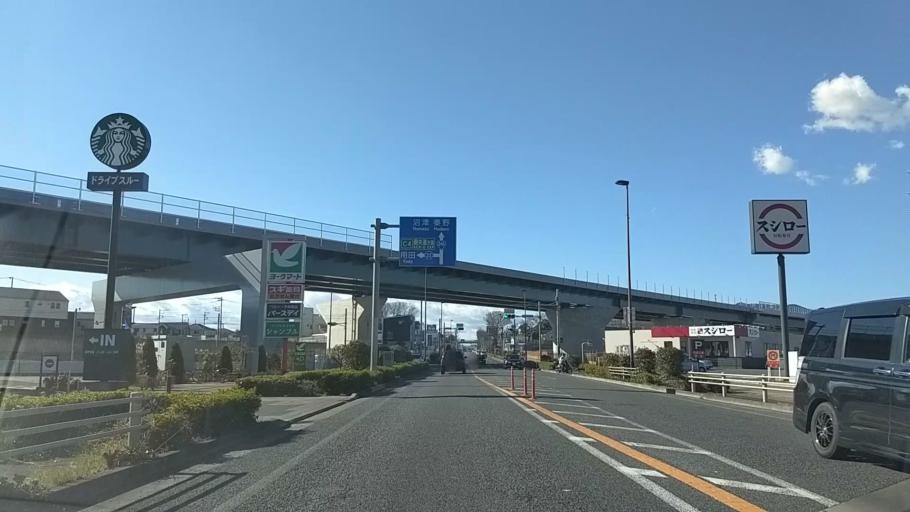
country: JP
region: Kanagawa
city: Isehara
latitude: 35.4088
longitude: 139.3246
